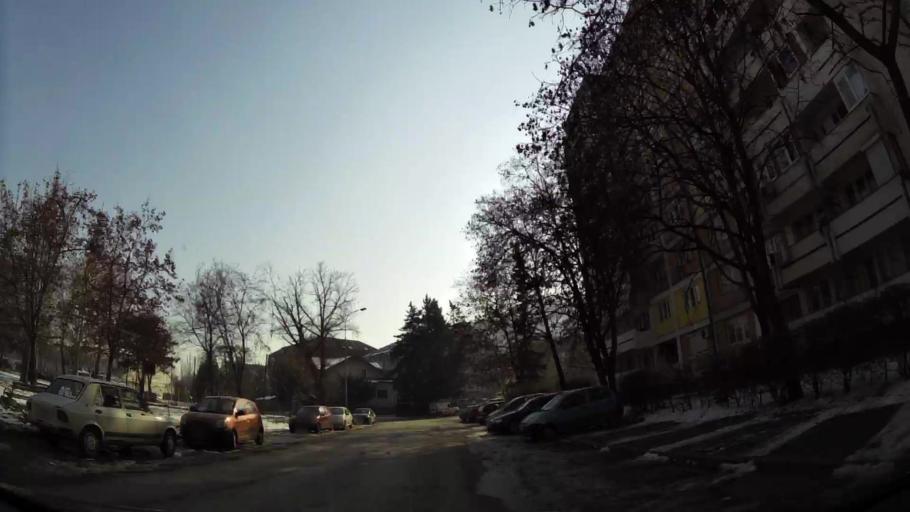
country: MK
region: Kisela Voda
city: Usje
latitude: 41.9726
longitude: 21.4418
